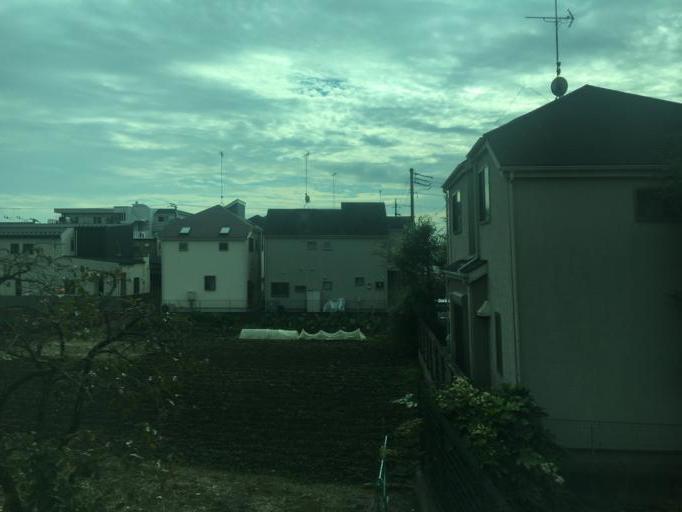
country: JP
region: Tokyo
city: Hino
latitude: 35.6844
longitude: 139.4361
